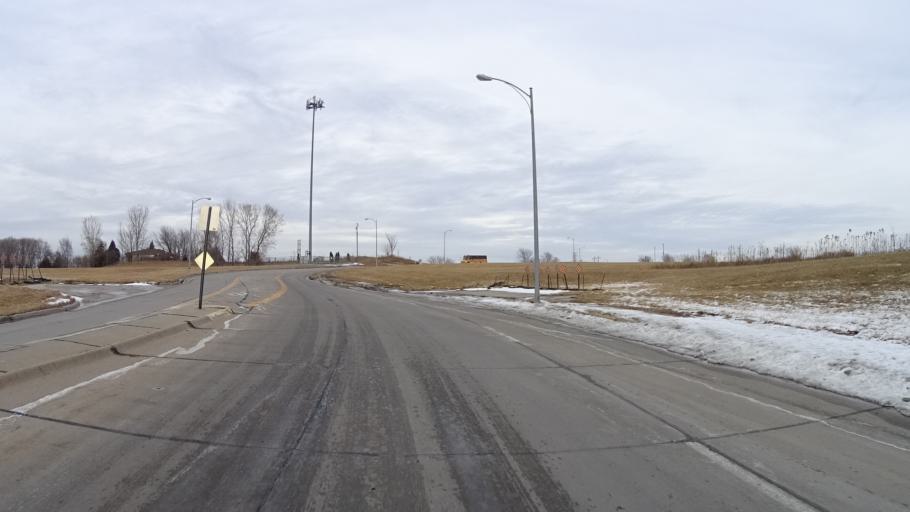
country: US
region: Nebraska
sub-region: Sarpy County
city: Offutt Air Force Base
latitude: 41.1527
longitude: -95.9260
